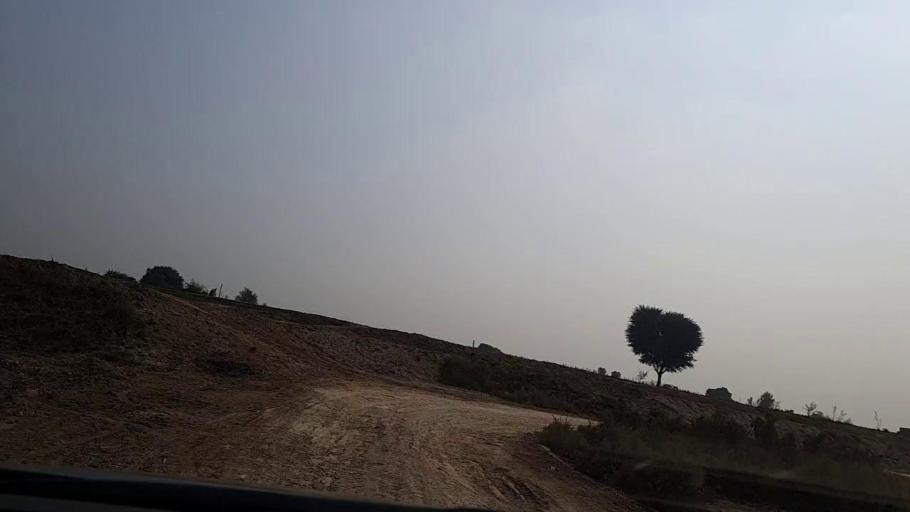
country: PK
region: Sindh
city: Sakrand
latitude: 26.1459
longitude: 68.2339
